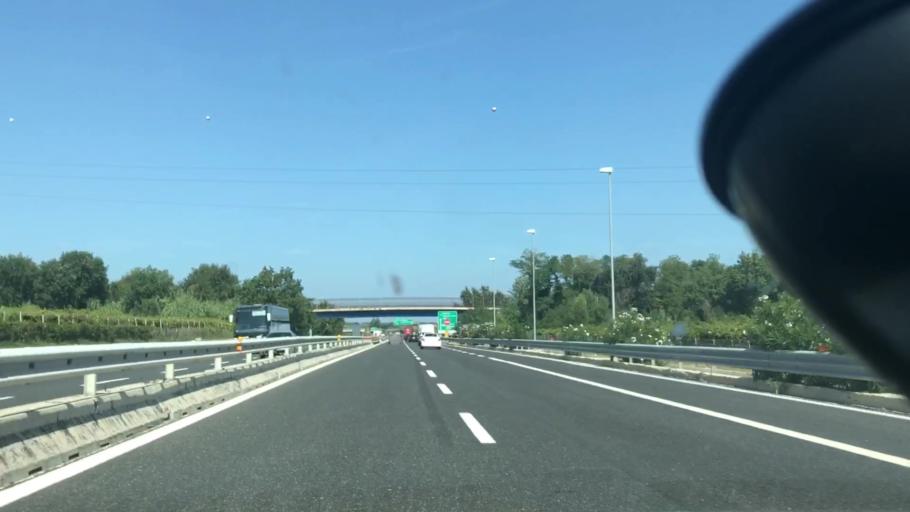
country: IT
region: Abruzzo
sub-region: Provincia di Chieti
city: Francavilla al Mare
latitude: 42.3899
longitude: 14.2887
